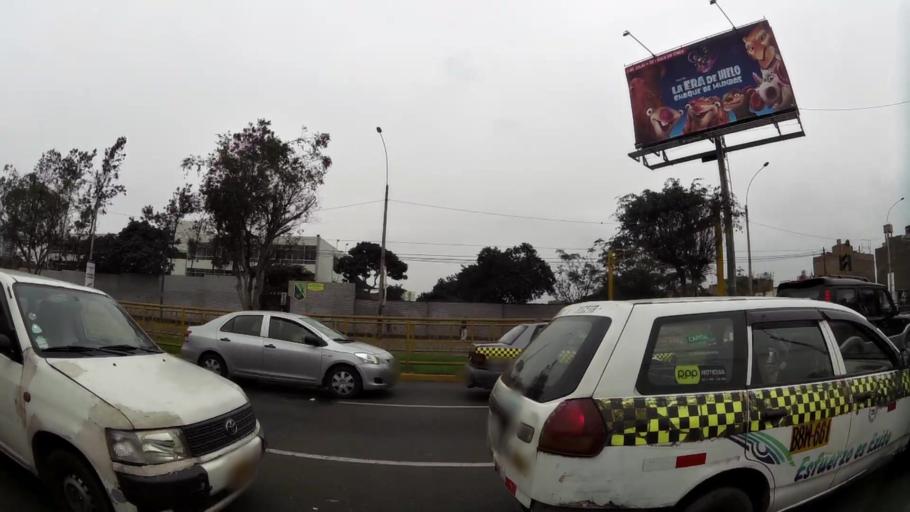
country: PE
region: Lima
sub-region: Lima
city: San Luis
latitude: -12.0816
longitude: -77.0219
